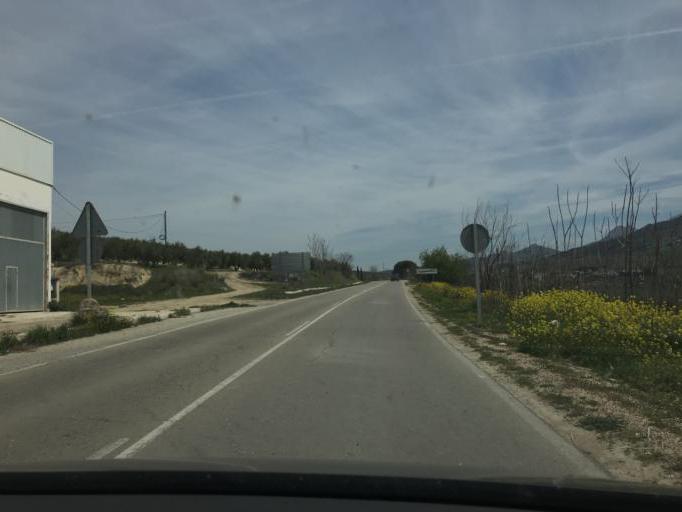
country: ES
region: Andalusia
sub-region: Provincia de Jaen
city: Jamilena
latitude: 37.7628
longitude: -3.9331
